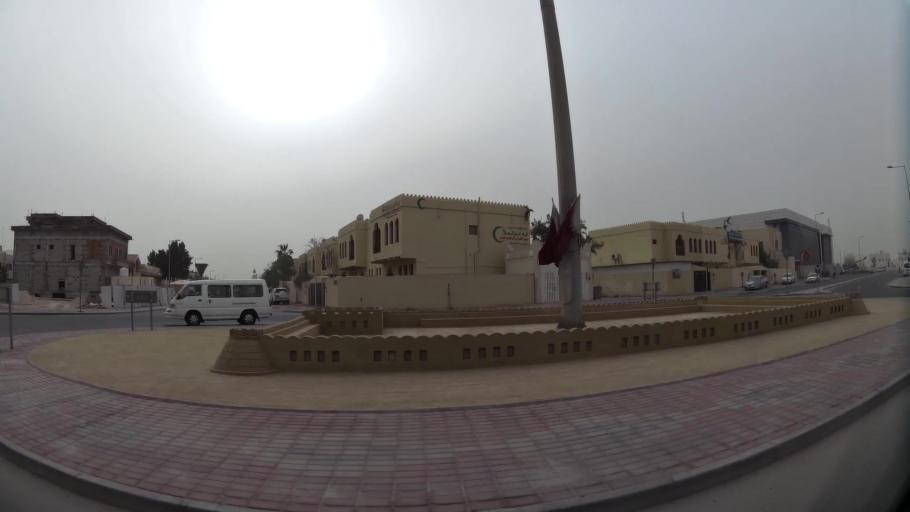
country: QA
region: Baladiyat ad Dawhah
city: Doha
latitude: 25.2561
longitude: 51.4990
